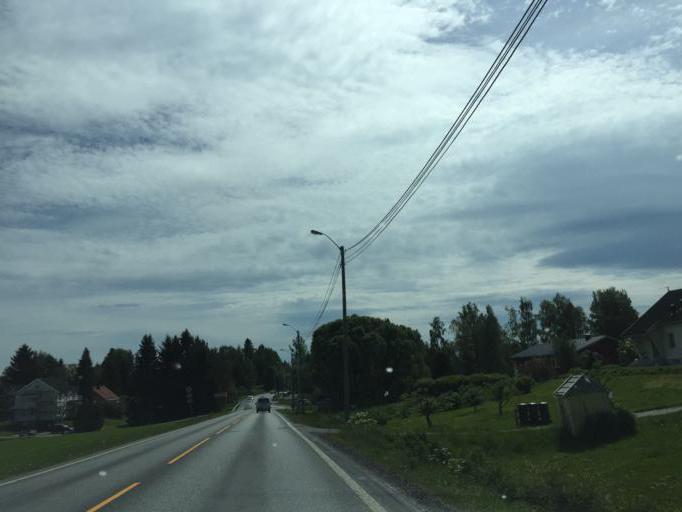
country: NO
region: Akershus
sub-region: Nes
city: Arnes
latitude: 60.1277
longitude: 11.4476
